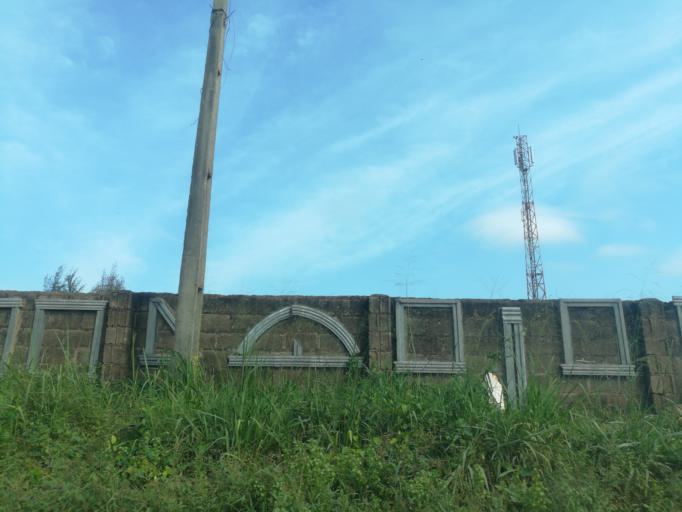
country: NG
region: Oyo
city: Ibadan
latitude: 7.3373
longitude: 3.8525
